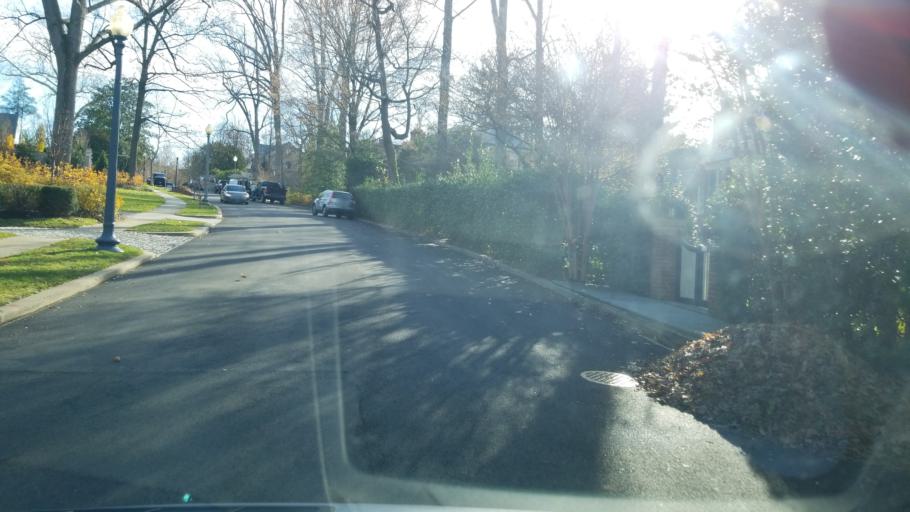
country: US
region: Maryland
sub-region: Montgomery County
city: Brookmont
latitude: 38.9348
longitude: -77.0977
